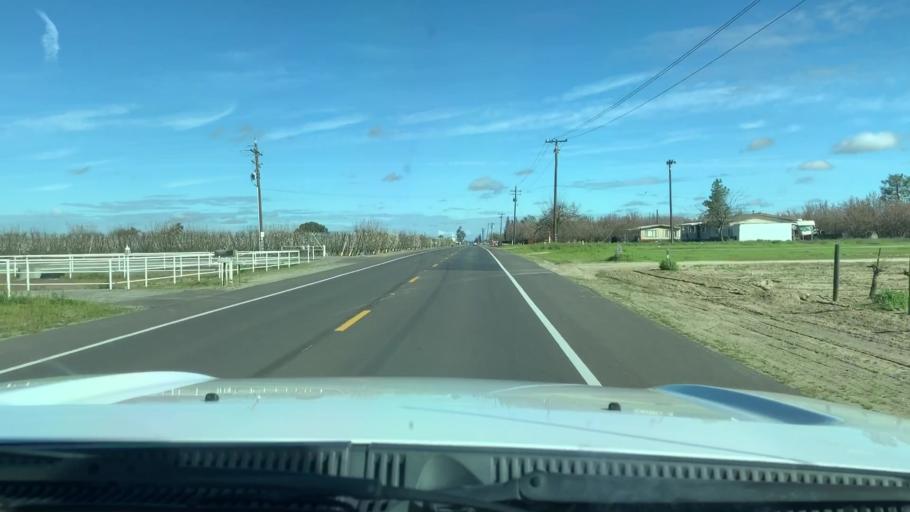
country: US
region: California
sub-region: Fresno County
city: Laton
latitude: 36.4978
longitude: -119.6830
